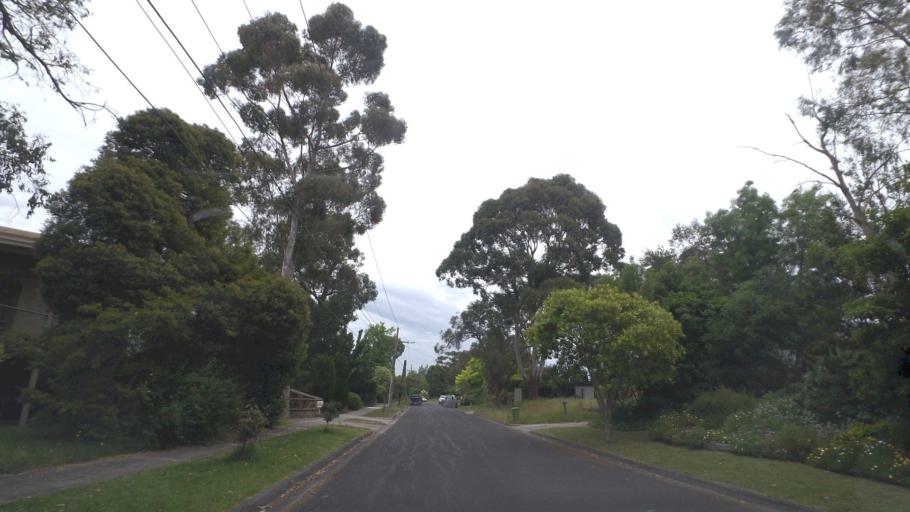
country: AU
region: Victoria
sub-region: Maroondah
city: Croydon North
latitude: -37.7977
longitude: 145.2947
